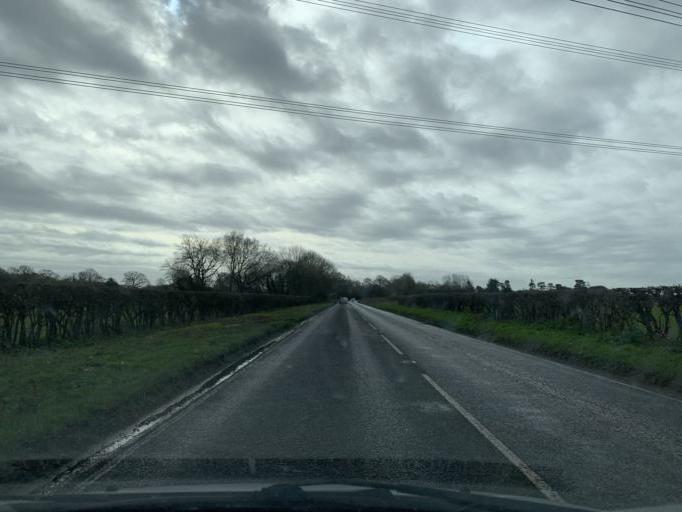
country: GB
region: England
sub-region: Hampshire
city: Fordingbridge
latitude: 50.9519
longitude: -1.7791
